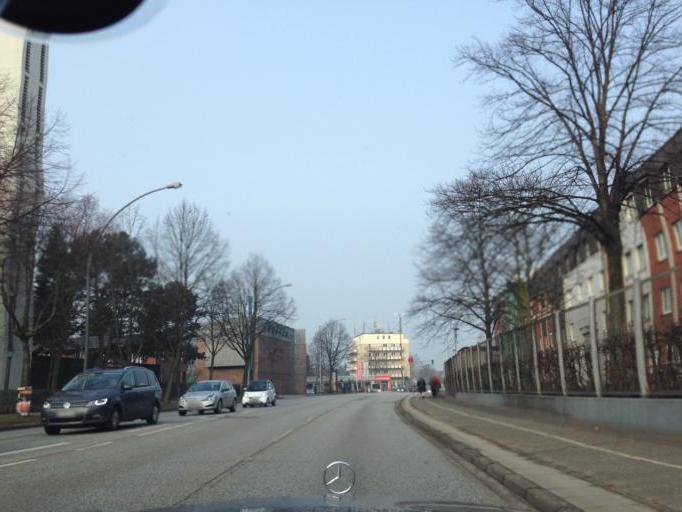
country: DE
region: Hamburg
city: Farmsen-Berne
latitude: 53.5847
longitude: 10.1253
